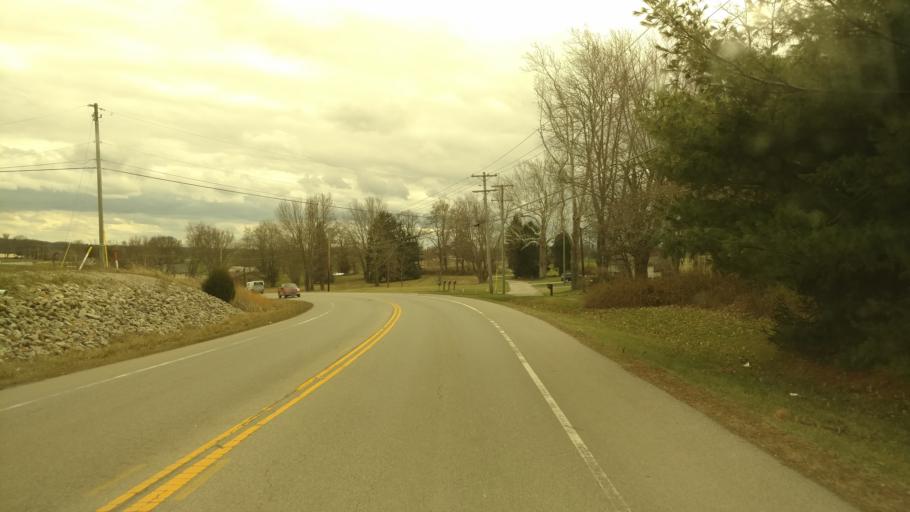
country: US
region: Ohio
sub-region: Muskingum County
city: North Zanesville
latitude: 40.0129
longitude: -82.0407
